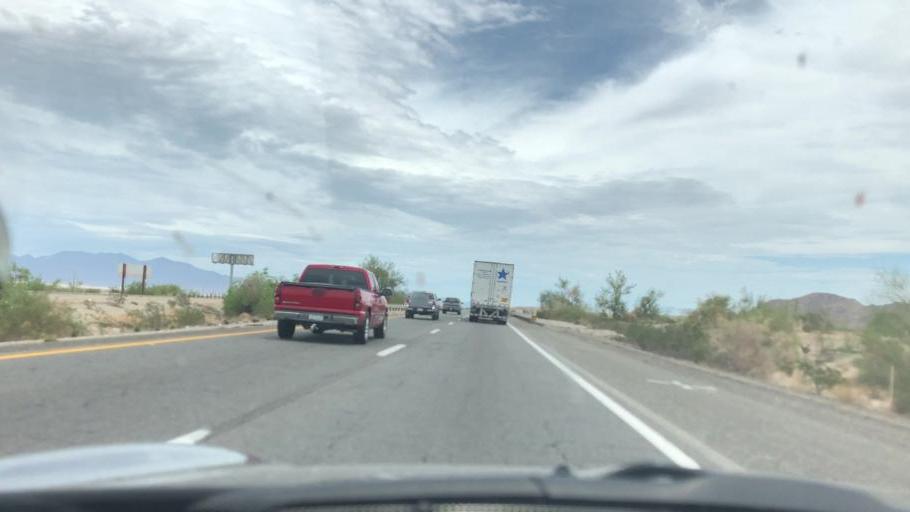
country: US
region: California
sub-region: Imperial County
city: Niland
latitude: 33.7100
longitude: -115.3754
